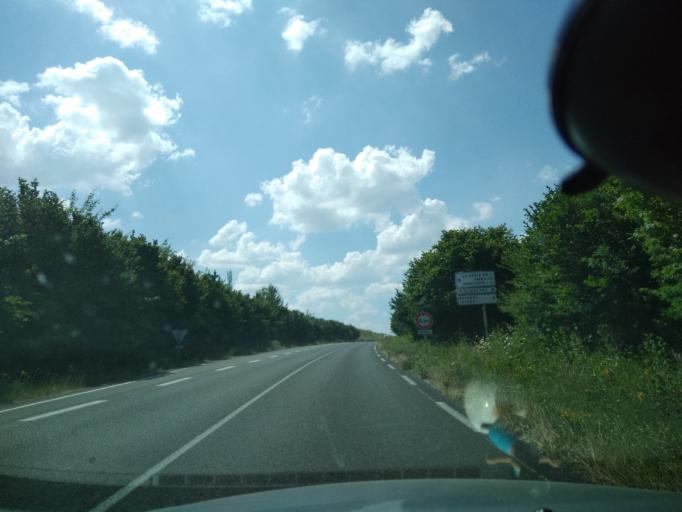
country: FR
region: Centre
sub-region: Departement d'Indre-et-Loire
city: Blere
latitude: 47.3148
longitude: 0.9945
